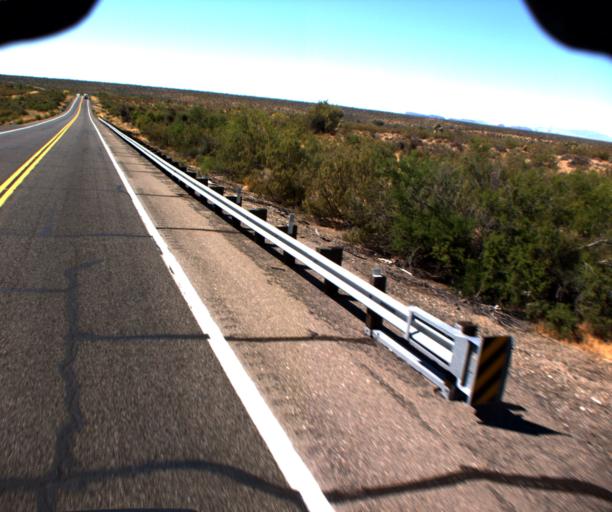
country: US
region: Arizona
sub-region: Yavapai County
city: Congress
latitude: 34.2141
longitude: -113.0667
